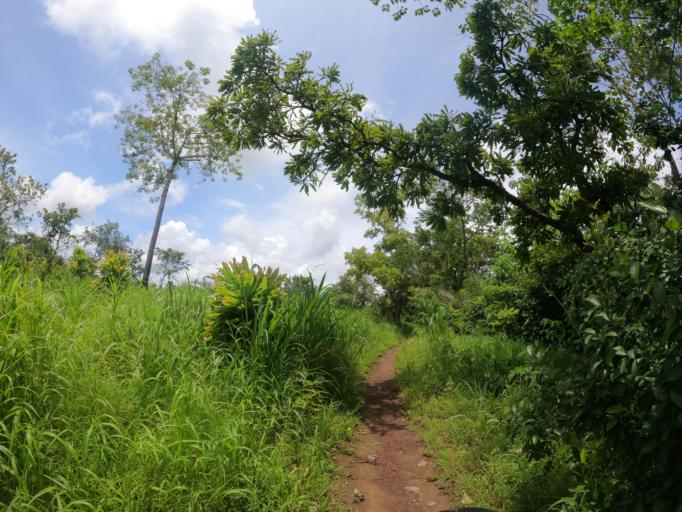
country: SL
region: Northern Province
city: Makeni
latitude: 9.1495
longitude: -12.2537
